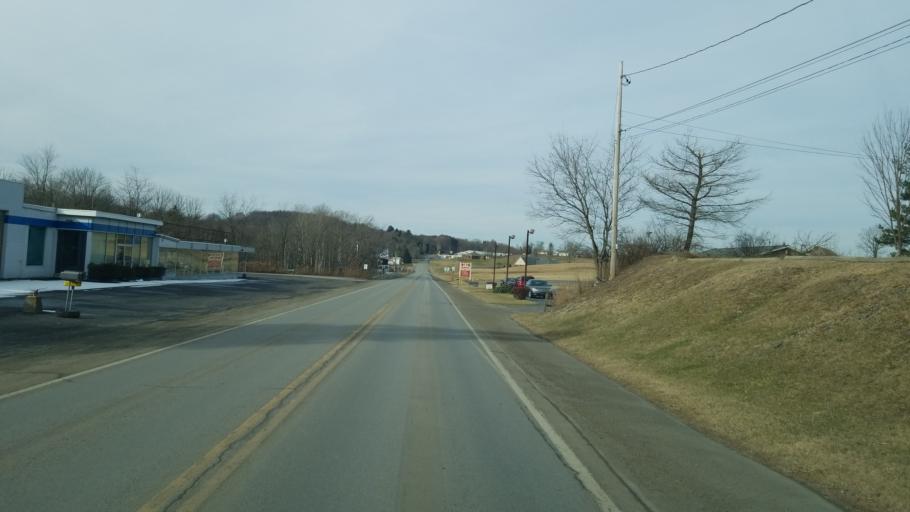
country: US
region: Pennsylvania
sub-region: Jefferson County
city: Punxsutawney
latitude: 40.9566
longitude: -79.0008
